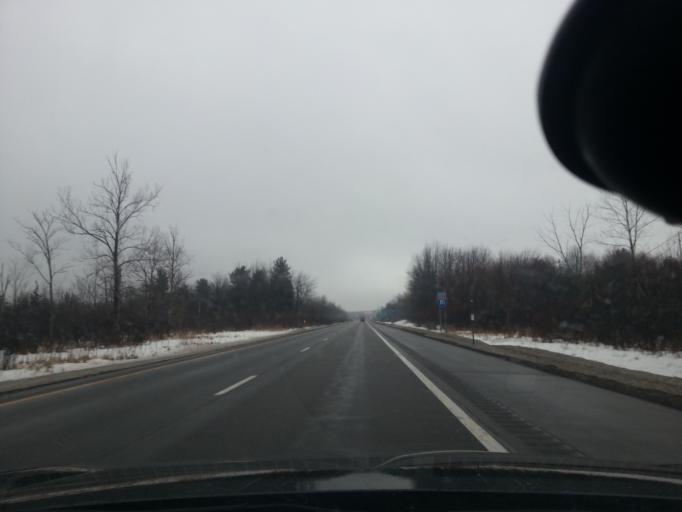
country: US
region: New York
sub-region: Oswego County
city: Pulaski
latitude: 43.6616
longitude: -76.0742
